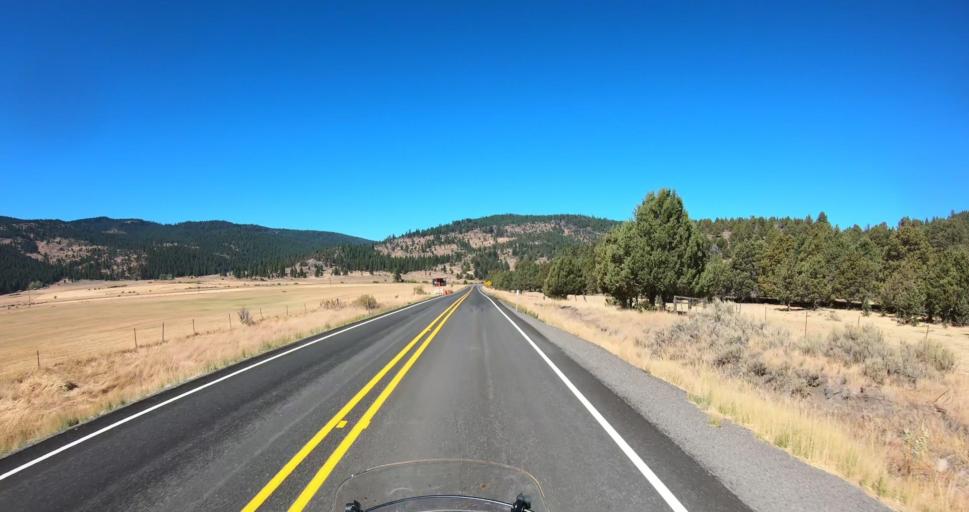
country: US
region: Oregon
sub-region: Lake County
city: Lakeview
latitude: 42.3799
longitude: -120.3024
